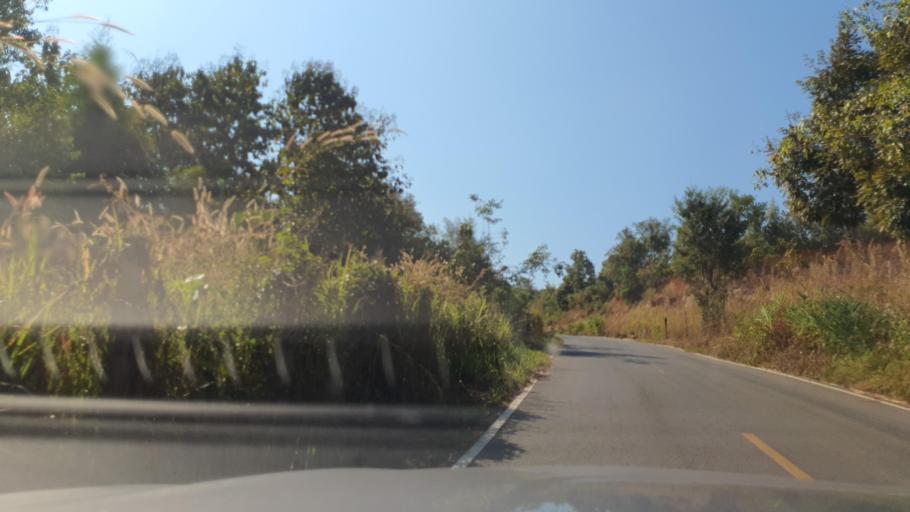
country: TH
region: Nan
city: Pua
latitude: 19.1610
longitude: 100.9070
